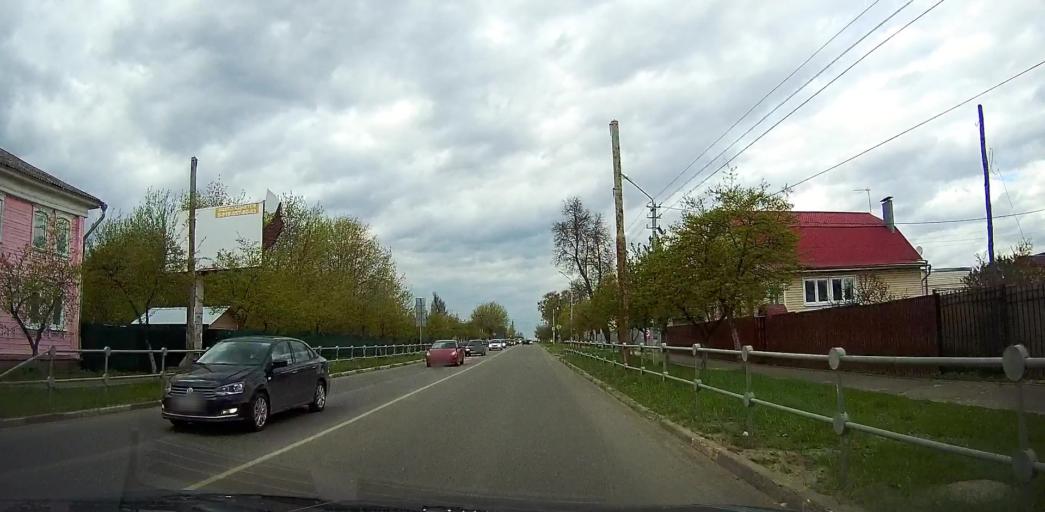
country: RU
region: Moskovskaya
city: Pavlovskiy Posad
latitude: 55.7862
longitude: 38.6477
